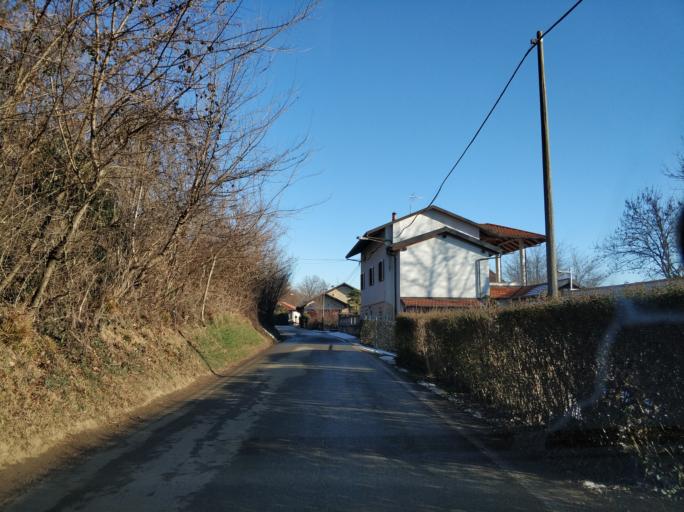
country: IT
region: Piedmont
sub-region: Provincia di Torino
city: San Francesco al Campo
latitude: 45.2205
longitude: 7.6674
